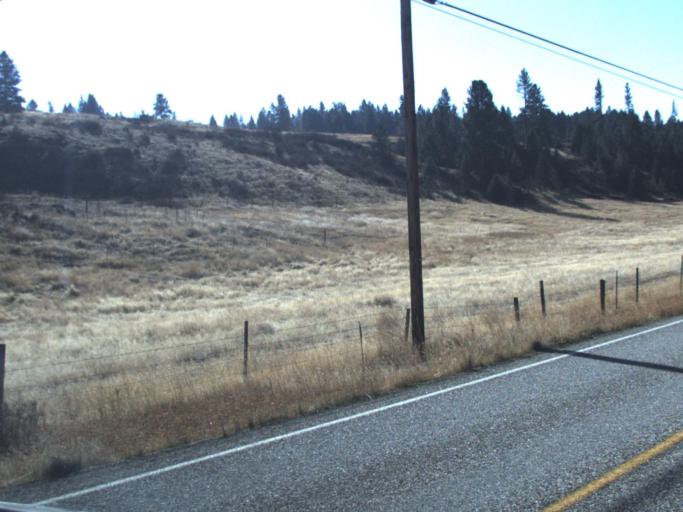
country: US
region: Washington
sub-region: Ferry County
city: Republic
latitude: 48.7487
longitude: -118.6547
